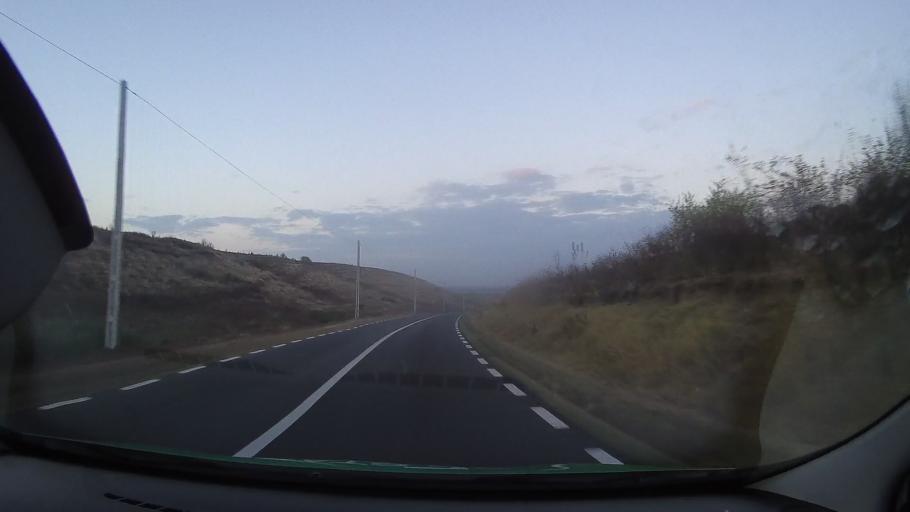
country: RO
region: Constanta
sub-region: Comuna Oltina
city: Oltina
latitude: 44.1384
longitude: 27.6654
